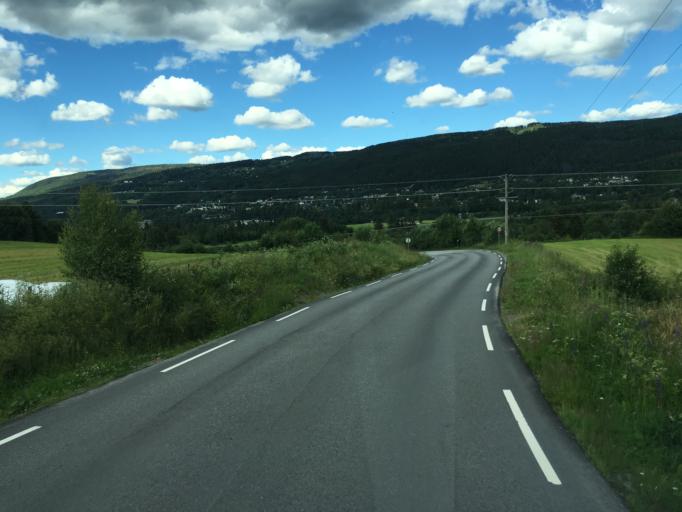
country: NO
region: Oppland
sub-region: Nordre Land
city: Dokka
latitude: 60.8205
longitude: 10.0741
